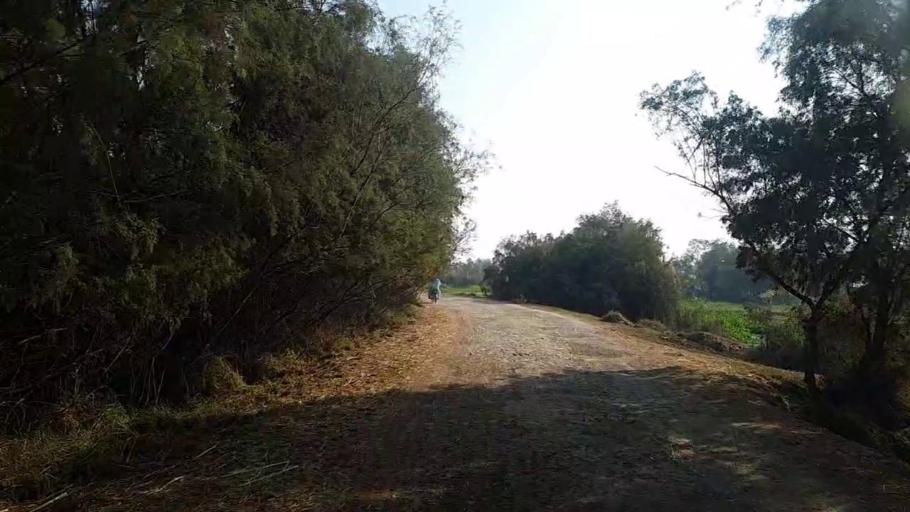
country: PK
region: Sindh
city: Mirpur Mathelo
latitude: 27.8952
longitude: 69.6071
